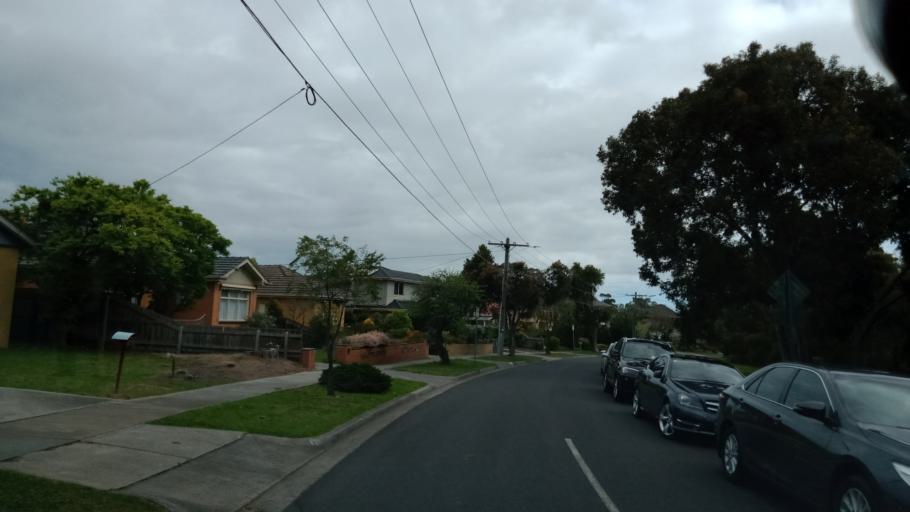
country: AU
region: Victoria
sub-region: Monash
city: Notting Hill
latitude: -37.8817
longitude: 145.1578
